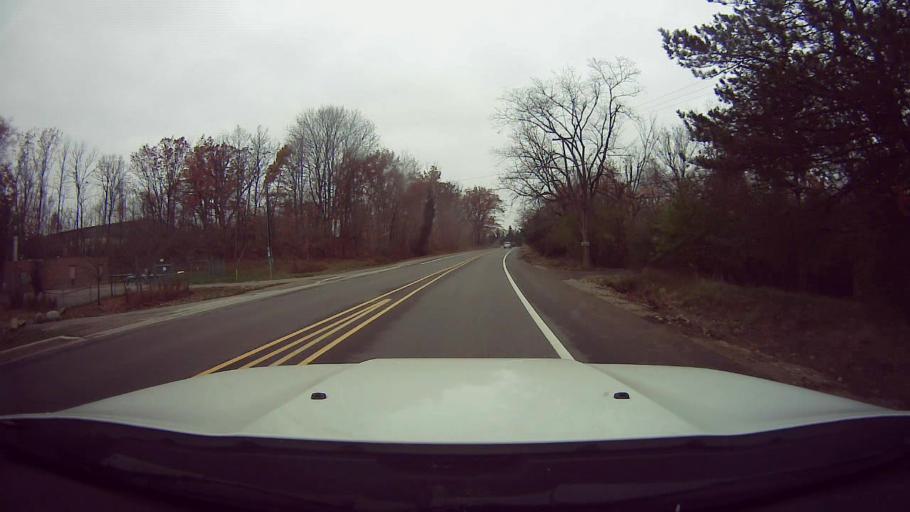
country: US
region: Michigan
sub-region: Oakland County
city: Bingham Farms
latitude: 42.5123
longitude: -83.2623
